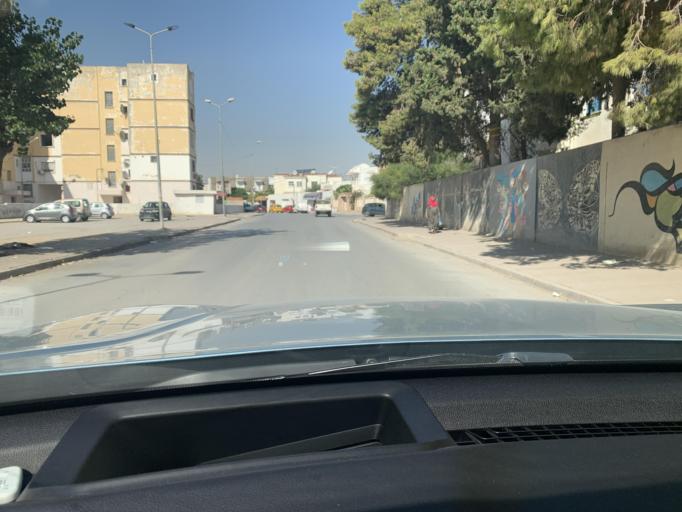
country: TN
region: Manouba
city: Manouba
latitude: 36.8251
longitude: 10.1185
